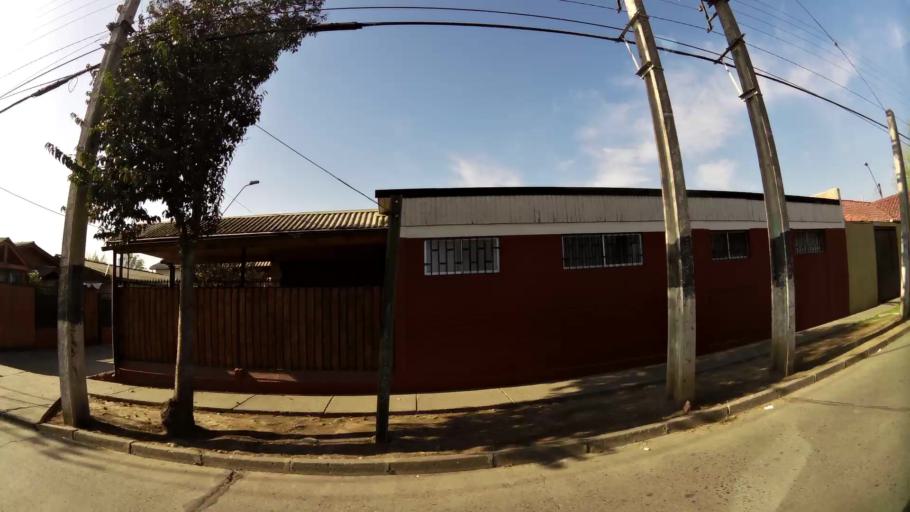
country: CL
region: Santiago Metropolitan
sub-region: Provincia de Santiago
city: Lo Prado
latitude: -33.3863
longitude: -70.6867
